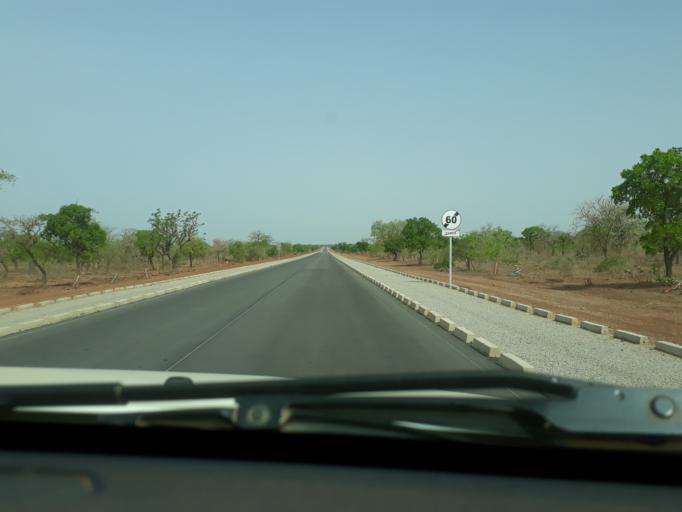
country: BF
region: Plateau-Central
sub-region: Province d'Oubritenga
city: Ziniare
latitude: 12.5502
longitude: -1.4063
